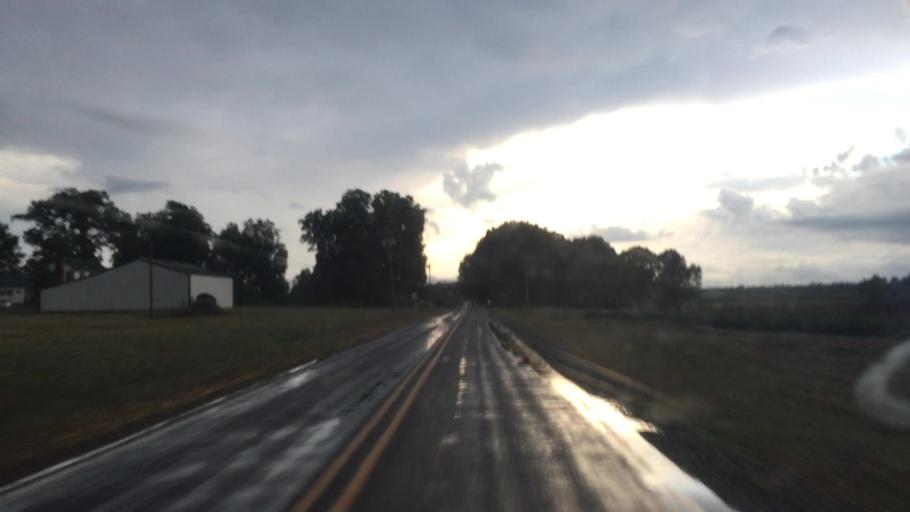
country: US
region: North Carolina
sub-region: Rowan County
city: Landis
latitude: 35.6424
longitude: -80.6684
